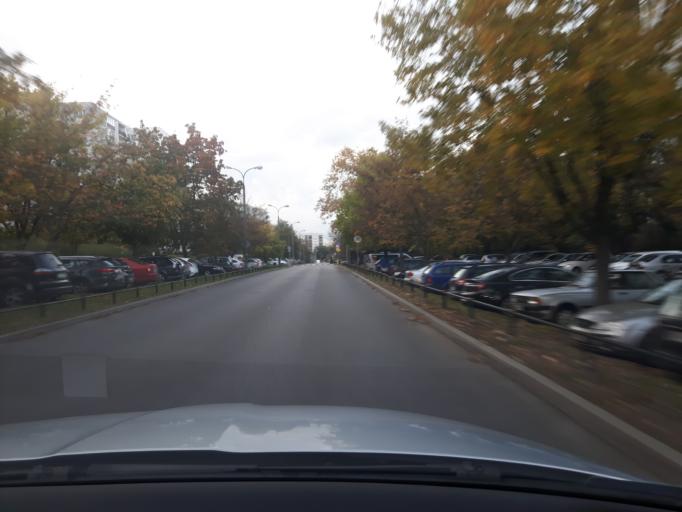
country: PL
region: Masovian Voivodeship
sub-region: Warszawa
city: Ursynow
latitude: 52.1402
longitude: 21.0520
